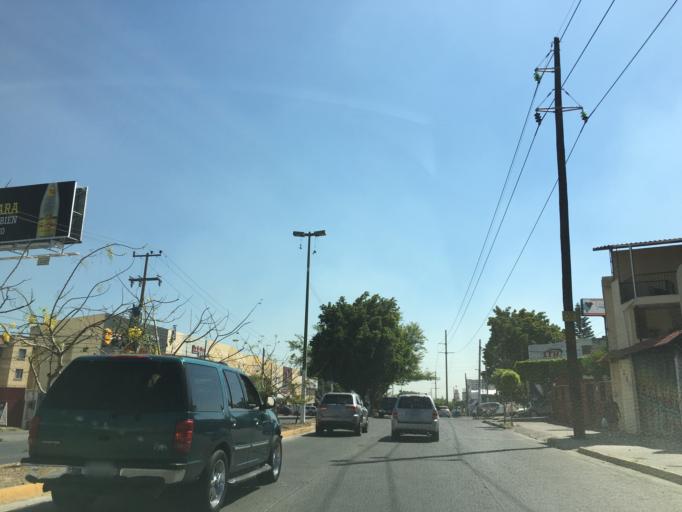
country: MX
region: Jalisco
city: Guadalajara
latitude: 20.6282
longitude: -103.4094
